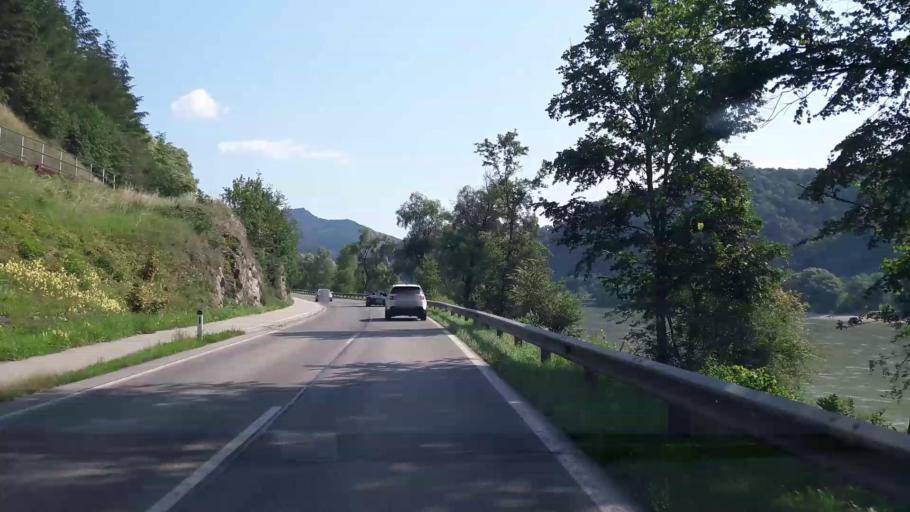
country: AT
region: Lower Austria
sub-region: Politischer Bezirk Krems
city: Aggsbach
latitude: 48.2822
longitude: 15.3960
